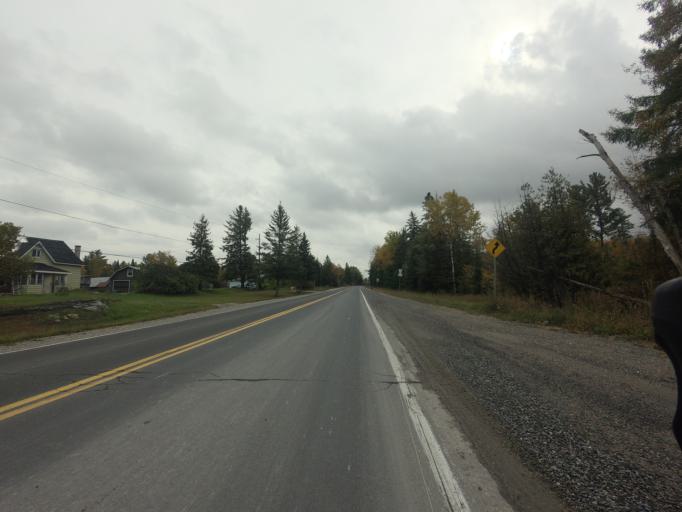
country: CA
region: Ontario
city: Perth
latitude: 45.1202
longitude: -76.4949
